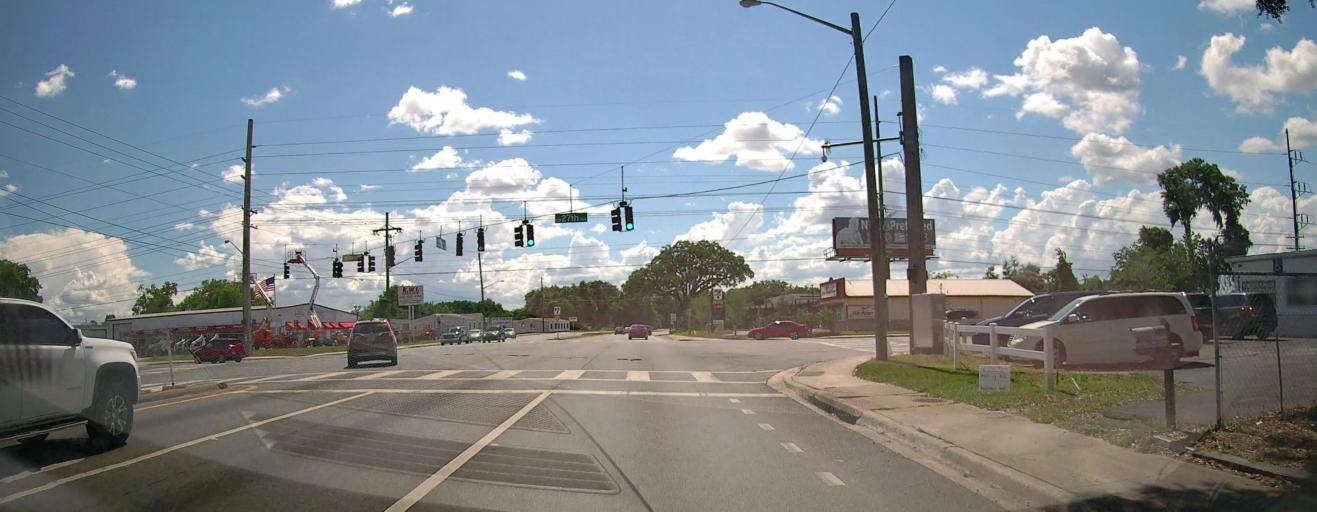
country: US
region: Florida
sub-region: Marion County
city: Ocala
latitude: 29.1963
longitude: -82.1676
